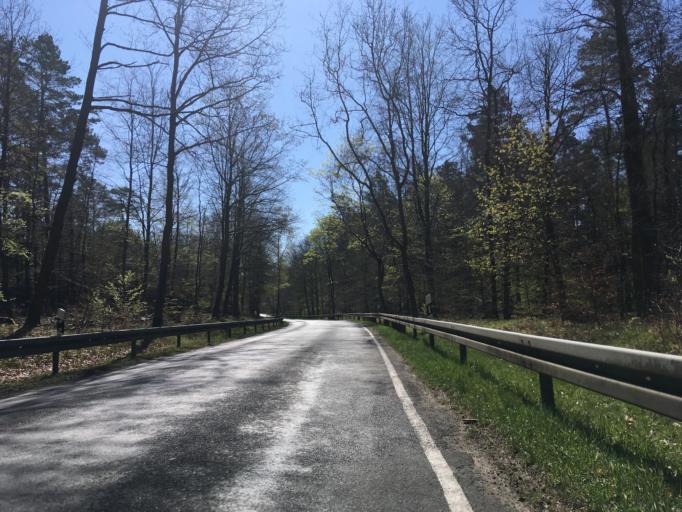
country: DE
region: Brandenburg
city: Bernau bei Berlin
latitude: 52.7173
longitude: 13.5735
